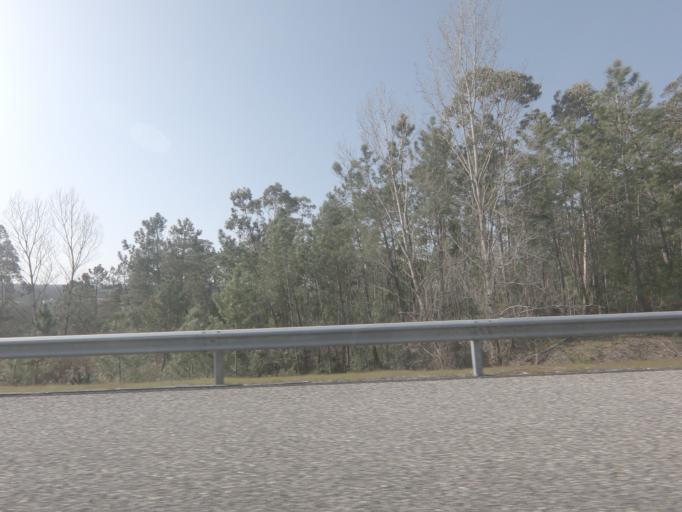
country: PT
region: Coimbra
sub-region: Soure
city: Soure
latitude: 40.0293
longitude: -8.5875
